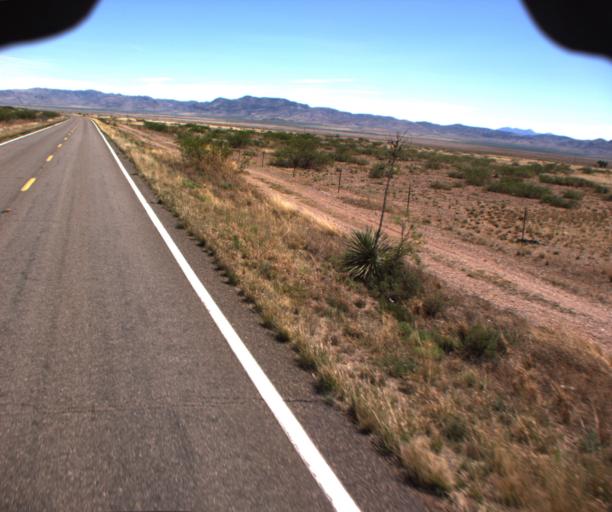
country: US
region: Arizona
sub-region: Cochise County
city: Douglas
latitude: 31.6395
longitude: -109.1798
